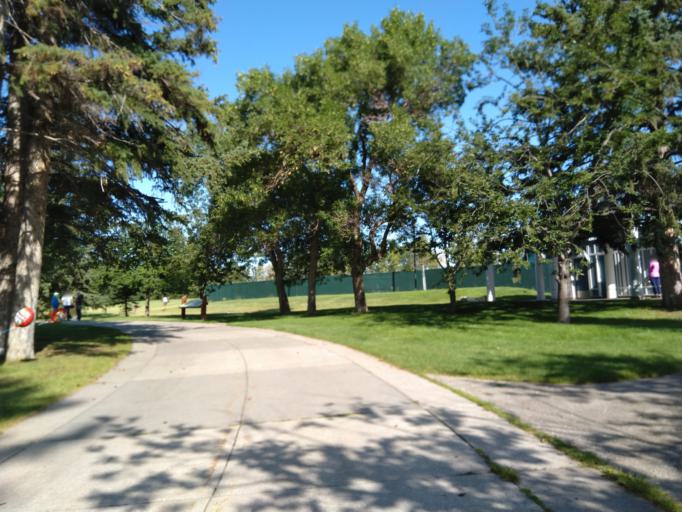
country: CA
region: Alberta
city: Calgary
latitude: 51.1008
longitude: -114.2205
